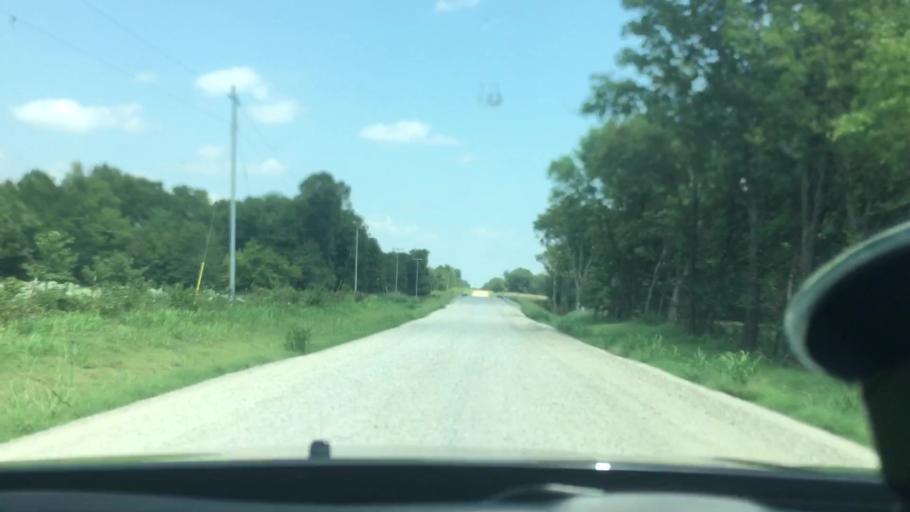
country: US
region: Oklahoma
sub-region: Coal County
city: Coalgate
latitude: 34.4266
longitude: -96.4638
